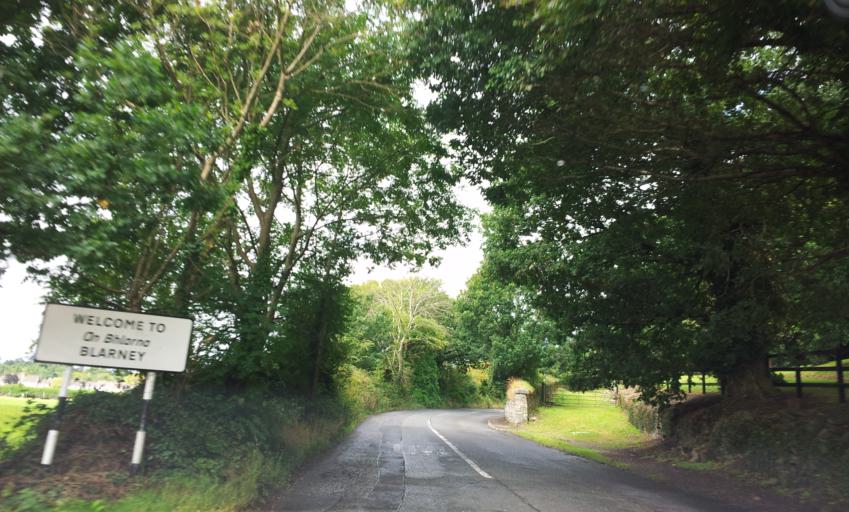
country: IE
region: Munster
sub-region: County Cork
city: Blarney
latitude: 51.9313
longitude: -8.5531
